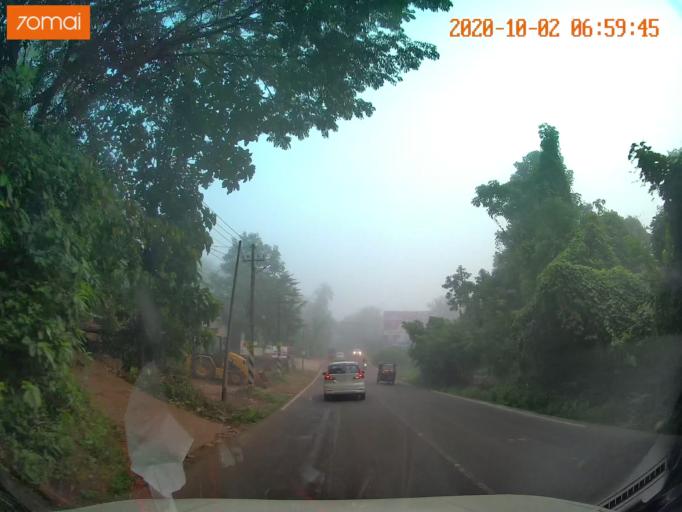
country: IN
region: Kerala
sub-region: Malappuram
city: Tirur
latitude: 10.8769
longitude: 76.0679
